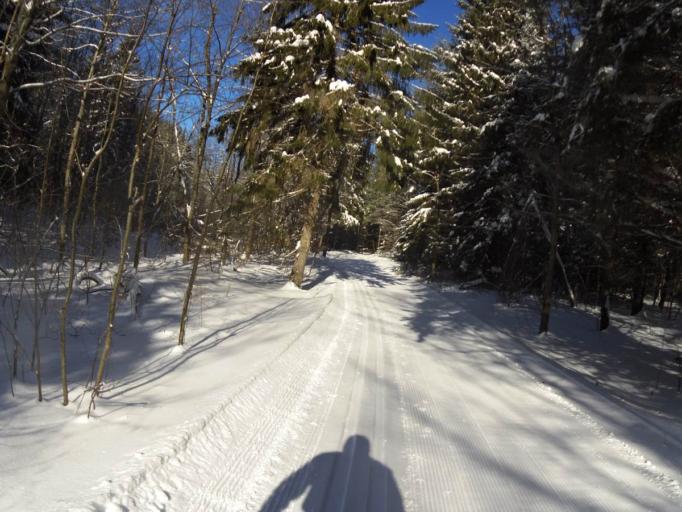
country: CA
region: Quebec
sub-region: Outaouais
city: Wakefield
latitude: 45.6206
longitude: -75.9455
